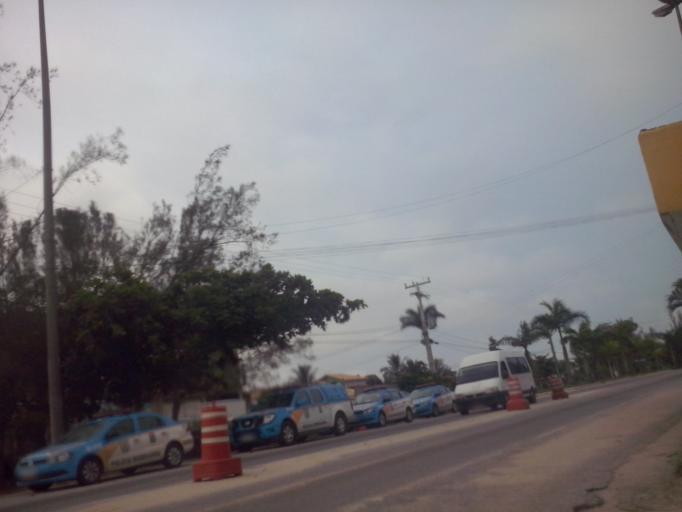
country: BR
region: Rio de Janeiro
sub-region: Rio Das Ostras
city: Rio das Ostras
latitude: -22.5616
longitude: -41.9817
